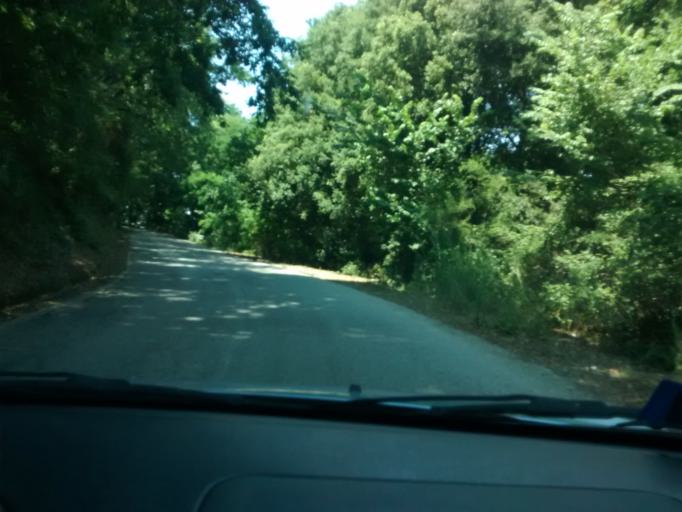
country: IT
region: Calabria
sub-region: Provincia di Catanzaro
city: Maida
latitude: 38.8991
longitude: 16.3956
